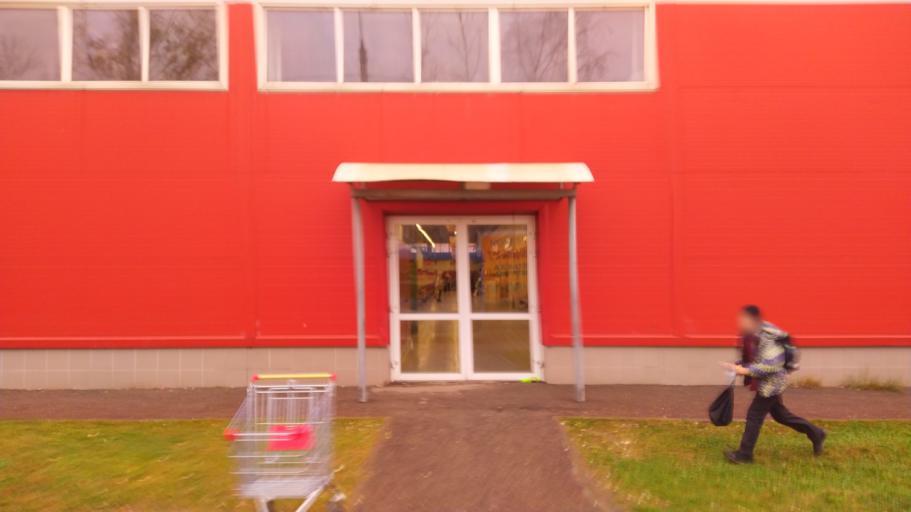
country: RU
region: Tverskaya
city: Tver
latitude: 56.8282
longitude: 35.8945
